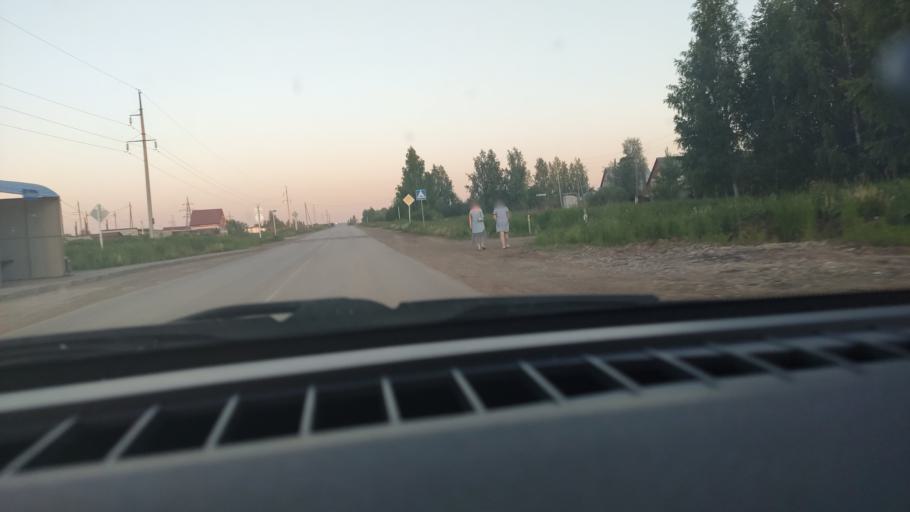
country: RU
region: Perm
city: Kultayevo
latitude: 57.8931
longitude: 55.9166
